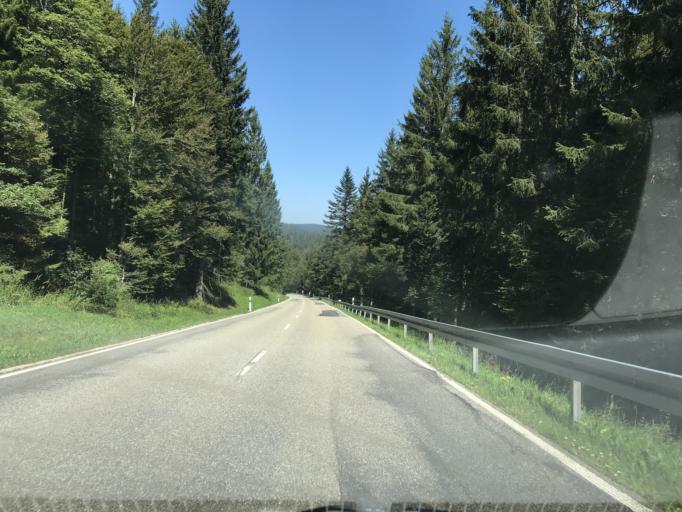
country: DE
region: Baden-Wuerttemberg
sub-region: Freiburg Region
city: Wieden
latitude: 47.8800
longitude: 7.9072
